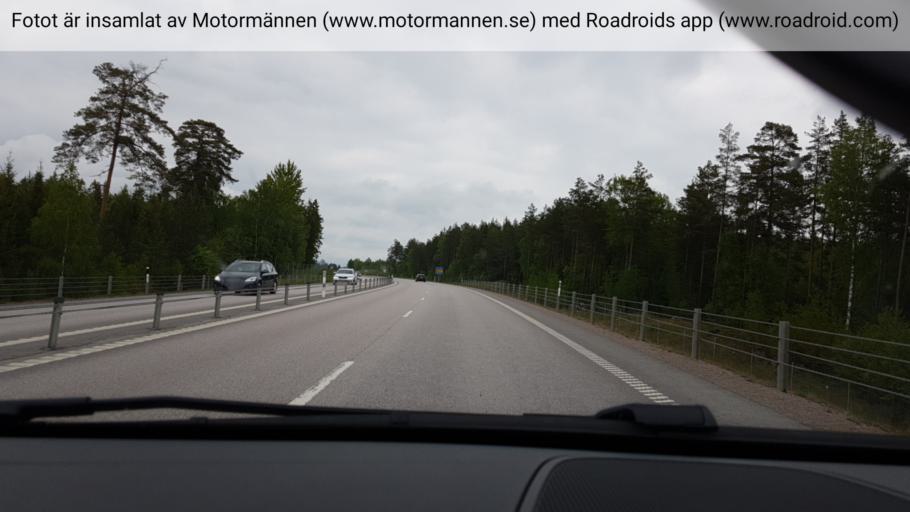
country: SE
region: Uppsala
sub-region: Uppsala Kommun
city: Storvreta
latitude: 59.9283
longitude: 17.7961
